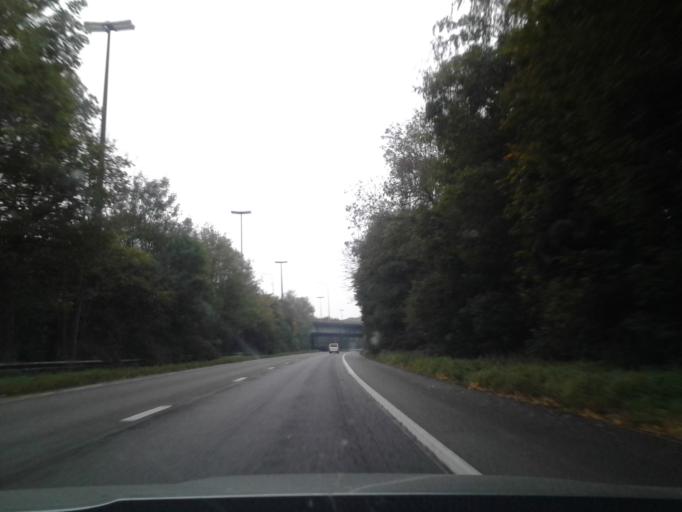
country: BE
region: Wallonia
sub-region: Province du Hainaut
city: La Louviere
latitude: 50.5046
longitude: 4.1649
